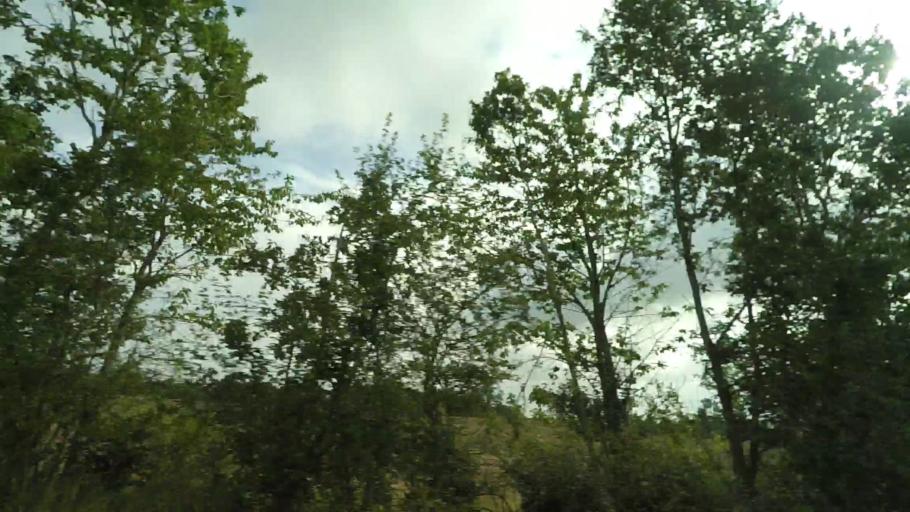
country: DK
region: Central Jutland
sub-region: Syddjurs Kommune
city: Ryomgard
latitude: 56.3643
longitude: 10.5089
